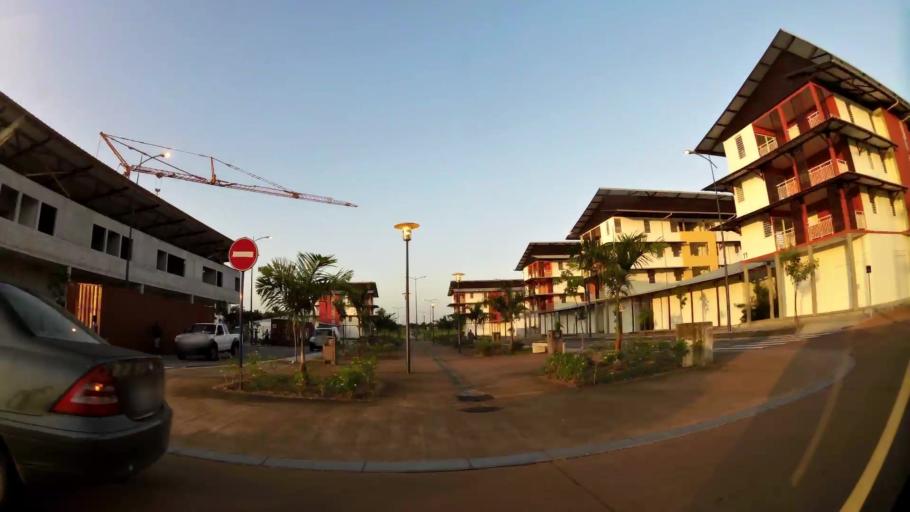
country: GF
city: Macouria
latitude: 4.9315
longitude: -52.4082
